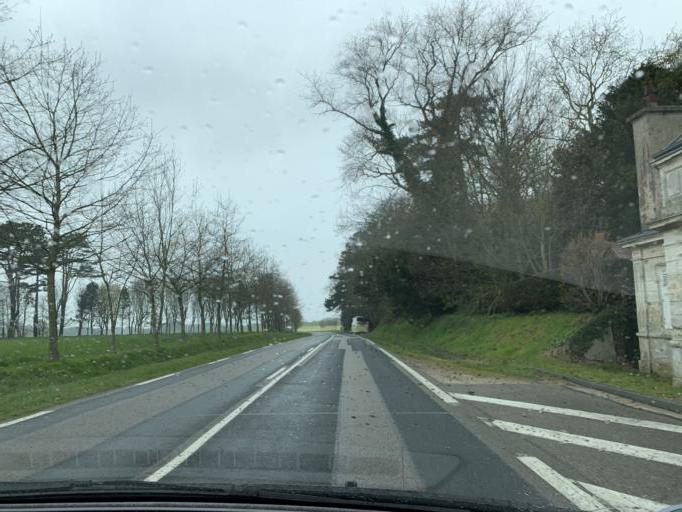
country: FR
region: Haute-Normandie
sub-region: Departement de la Seine-Maritime
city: Etretat
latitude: 49.6926
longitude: 0.2054
